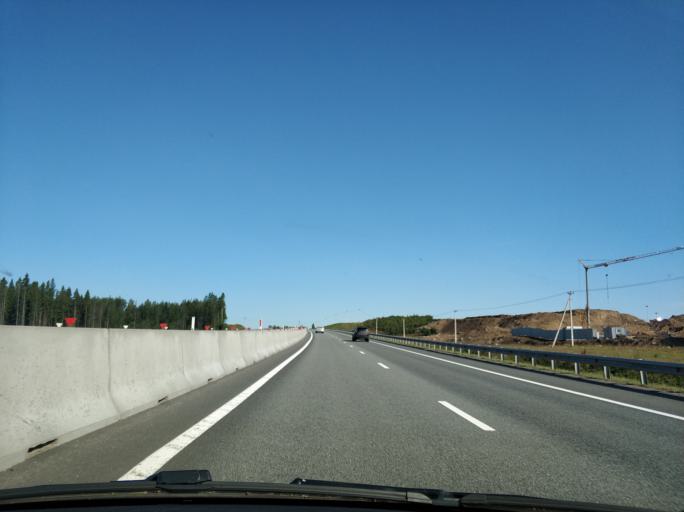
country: RU
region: Leningrad
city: Sosnovo
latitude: 60.5103
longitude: 30.1893
